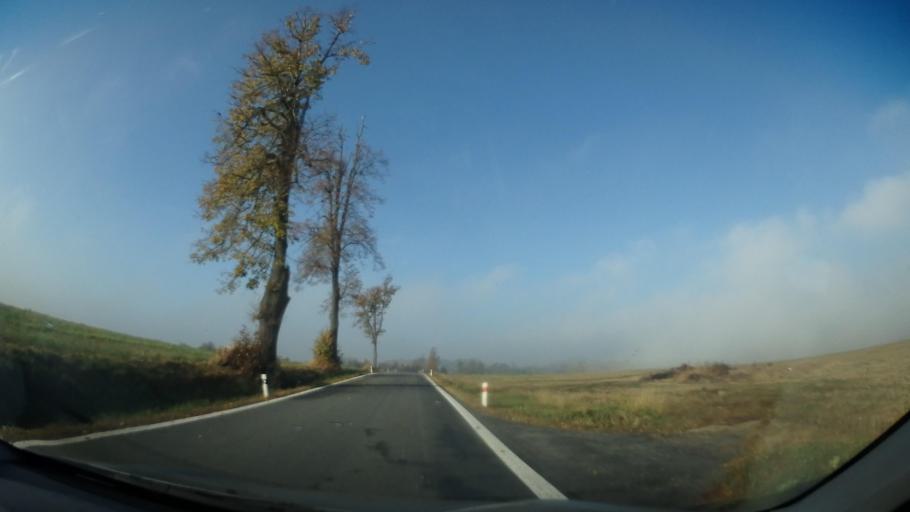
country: CZ
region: Vysocina
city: Krizanov
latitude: 49.4385
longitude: 16.1608
